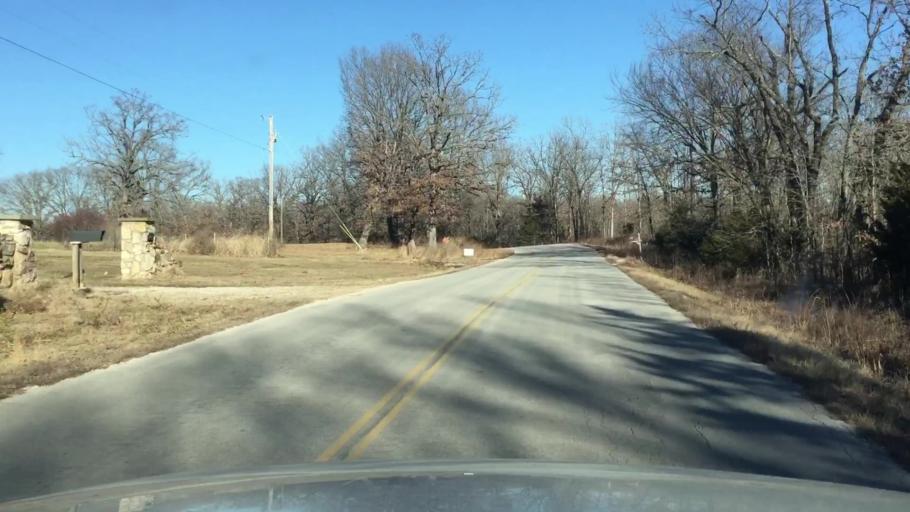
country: US
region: Missouri
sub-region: Morgan County
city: Versailles
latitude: 38.3423
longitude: -92.7504
